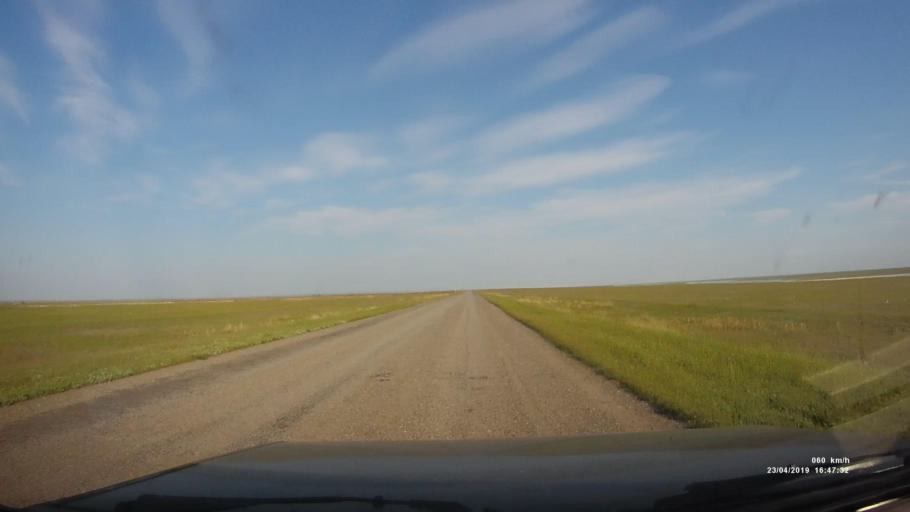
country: RU
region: Kalmykiya
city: Priyutnoye
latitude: 46.3385
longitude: 43.2492
